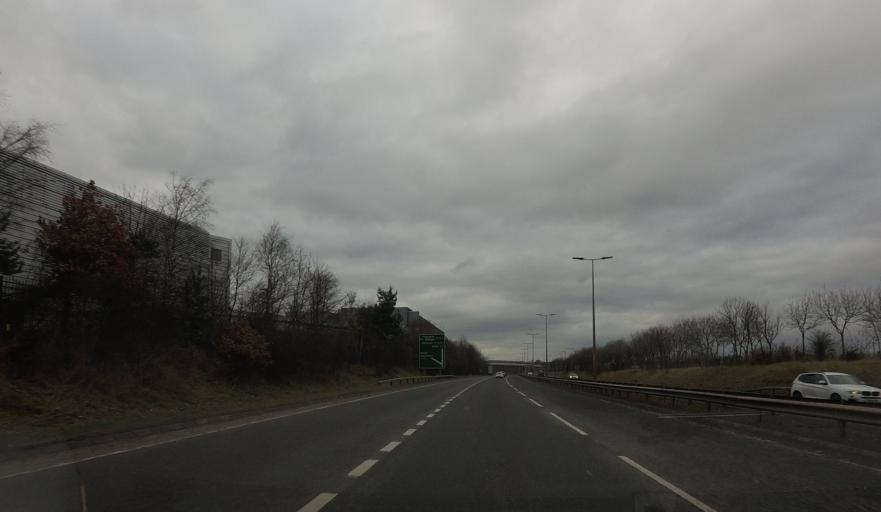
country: GB
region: Scotland
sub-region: Highland
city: Inverness
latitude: 57.4757
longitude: -4.1875
